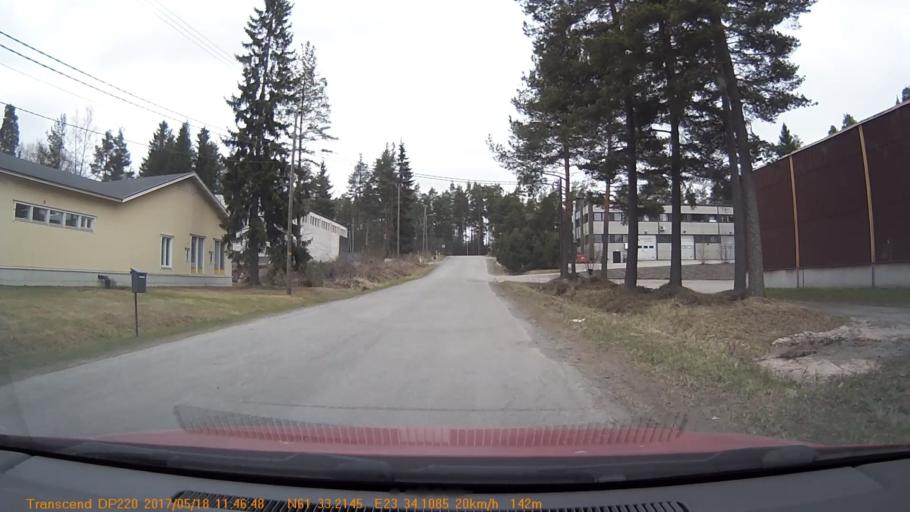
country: FI
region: Pirkanmaa
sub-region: Tampere
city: Yloejaervi
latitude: 61.5534
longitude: 23.5683
